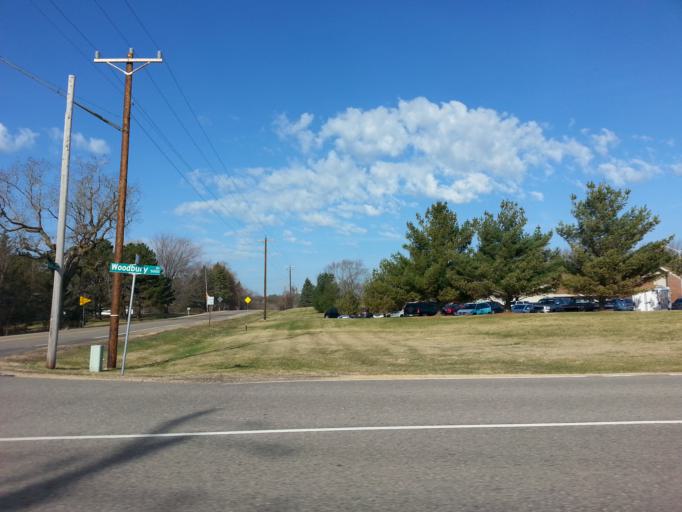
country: US
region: Minnesota
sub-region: Washington County
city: Cottage Grove
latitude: 44.8765
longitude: -92.9031
